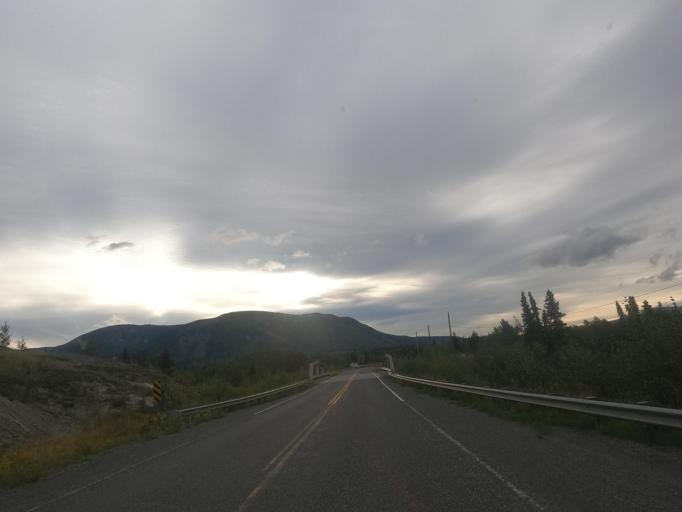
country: CA
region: Yukon
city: Haines Junction
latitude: 60.8589
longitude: -137.0656
